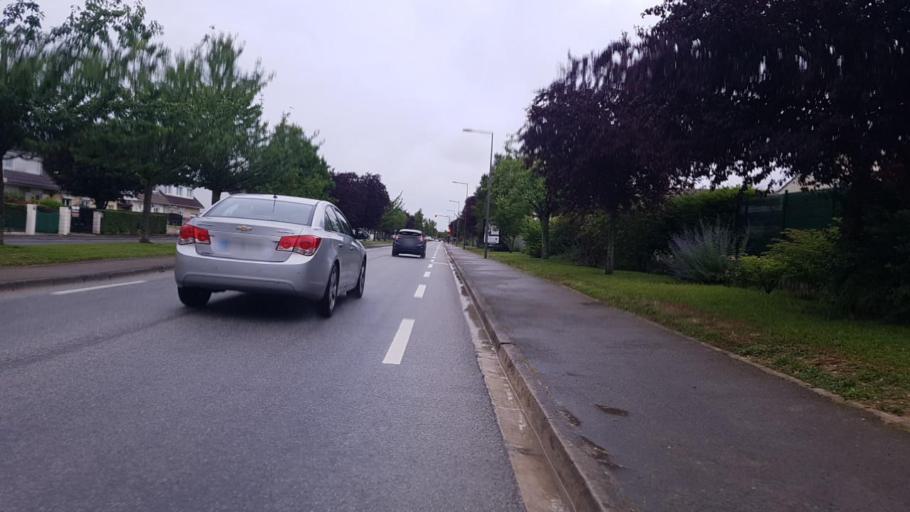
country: FR
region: Champagne-Ardenne
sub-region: Departement de la Marne
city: Saint-Memmie
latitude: 48.9352
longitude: 4.3873
